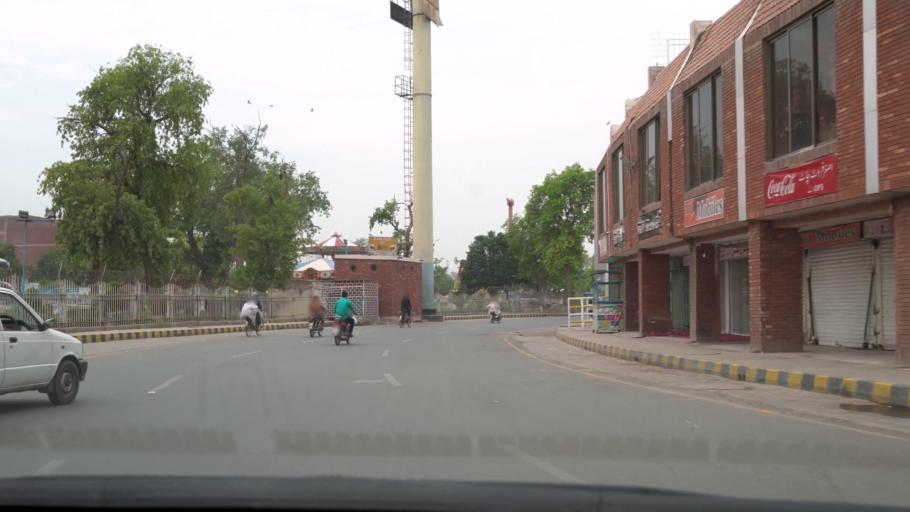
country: PK
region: Punjab
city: Faisalabad
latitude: 31.4330
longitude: 73.0840
